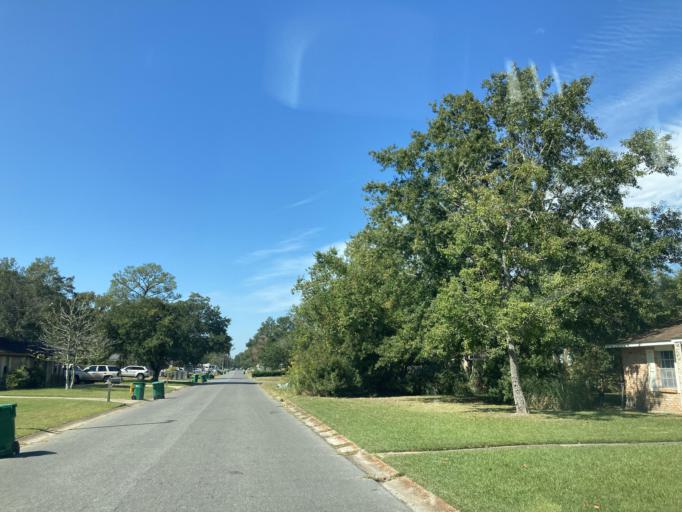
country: US
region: Mississippi
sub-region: Jackson County
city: Saint Martin
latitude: 30.4508
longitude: -88.8684
